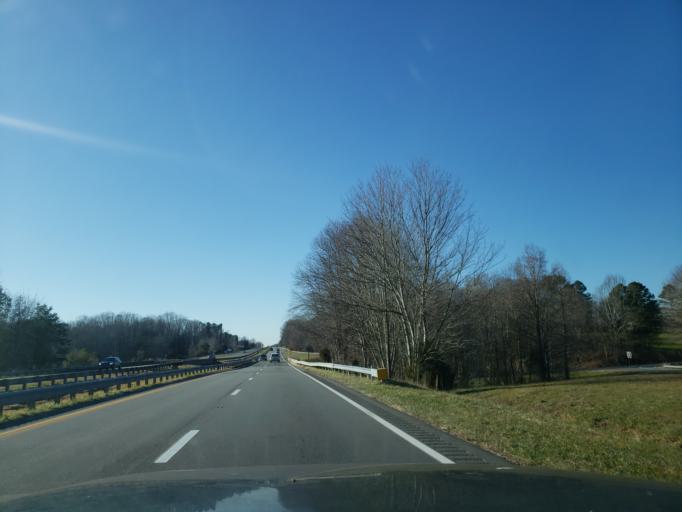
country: US
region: North Carolina
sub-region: Yadkin County
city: Yadkinville
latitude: 36.1133
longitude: -80.5873
